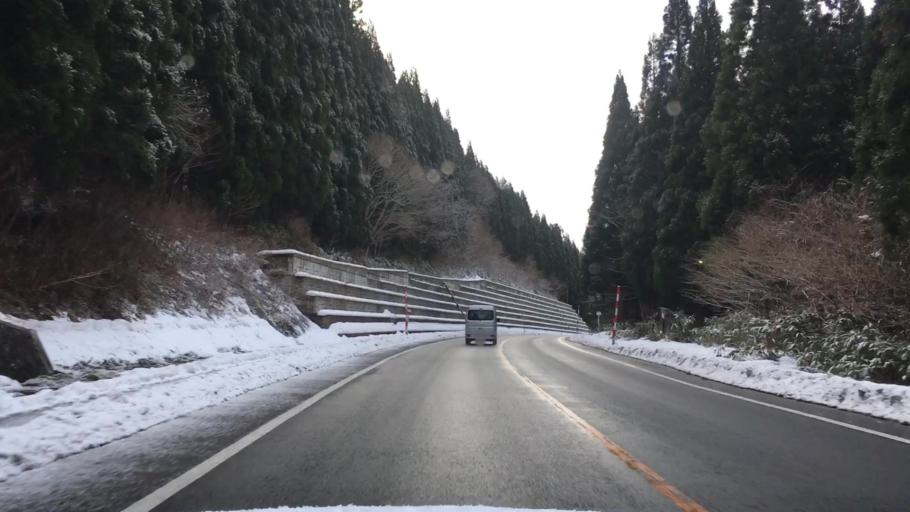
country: JP
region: Akita
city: Odate
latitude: 40.3888
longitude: 140.6051
